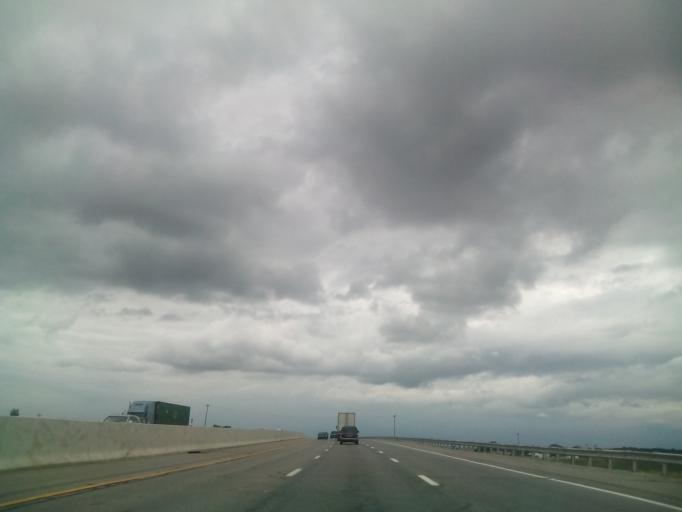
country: US
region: Ohio
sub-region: Wood County
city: Walbridge
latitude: 41.5404
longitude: -83.5159
